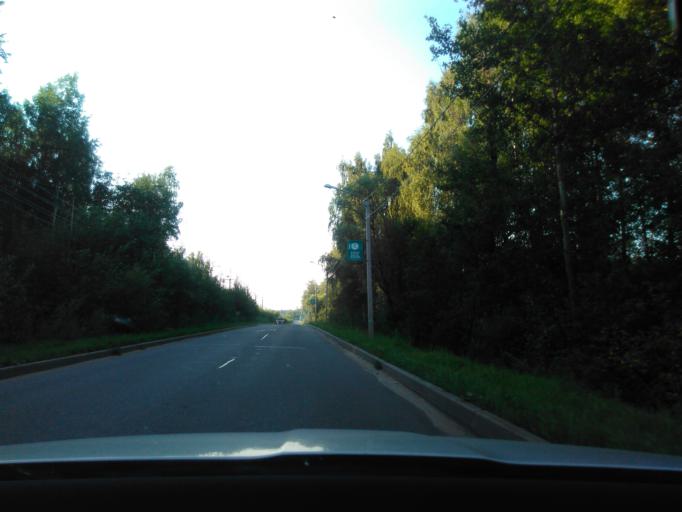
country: RU
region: Tverskaya
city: Konakovo
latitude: 56.7322
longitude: 36.7841
